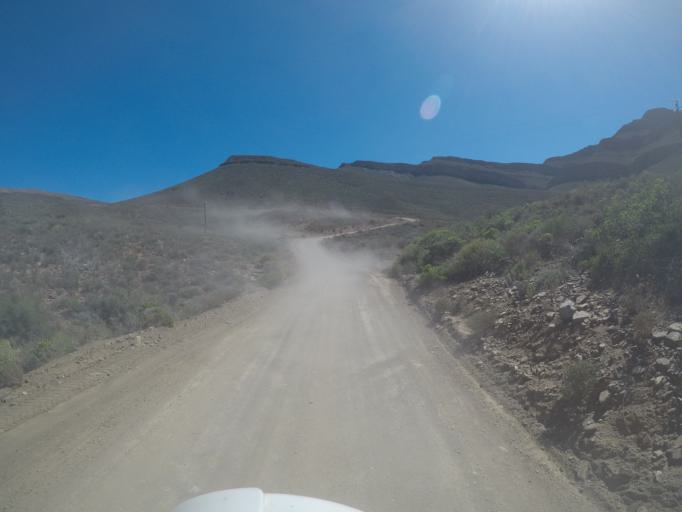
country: ZA
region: Western Cape
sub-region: West Coast District Municipality
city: Clanwilliam
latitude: -32.6204
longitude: 19.3844
